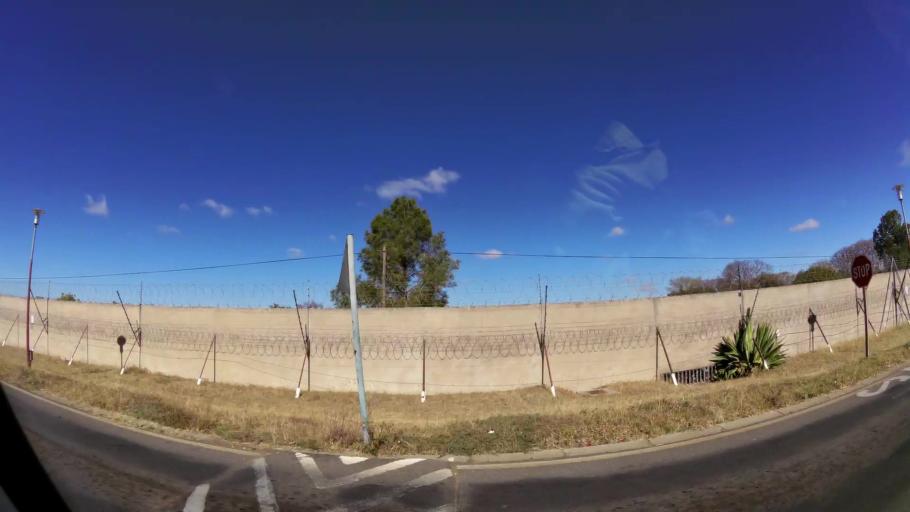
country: ZA
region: Limpopo
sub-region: Capricorn District Municipality
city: Polokwane
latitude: -23.8629
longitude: 29.4561
